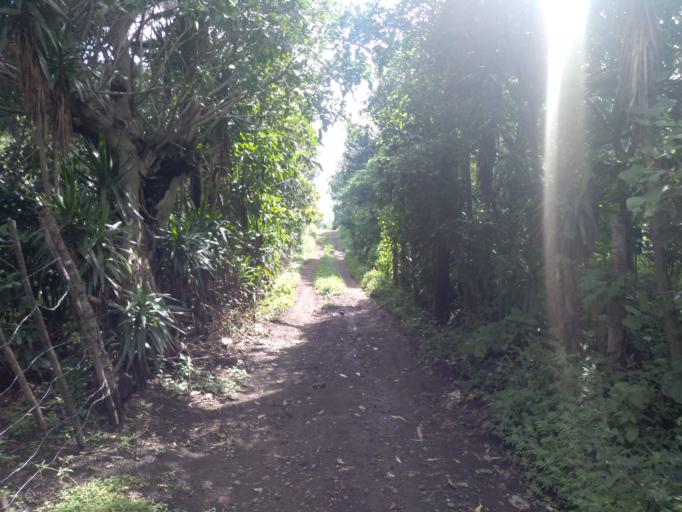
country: GT
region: Escuintla
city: San Vicente Pacaya
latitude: 14.3739
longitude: -90.5662
